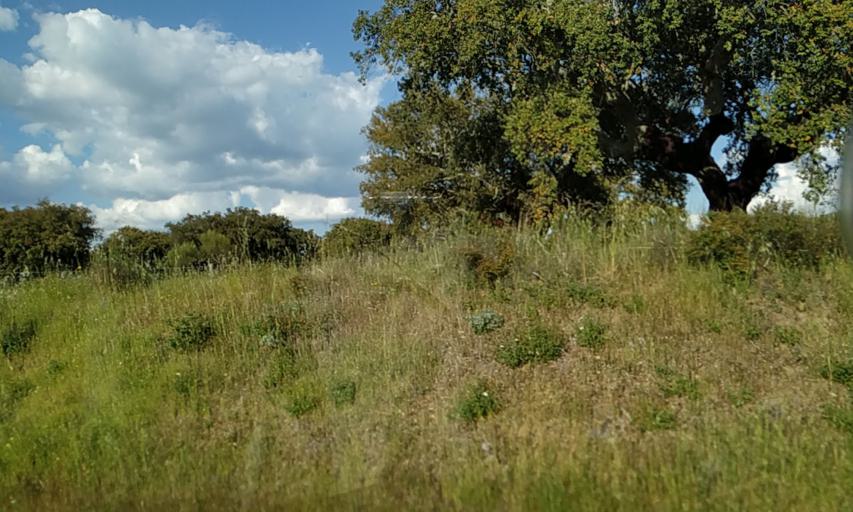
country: PT
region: Portalegre
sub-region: Portalegre
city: Urra
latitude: 39.1517
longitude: -7.4542
